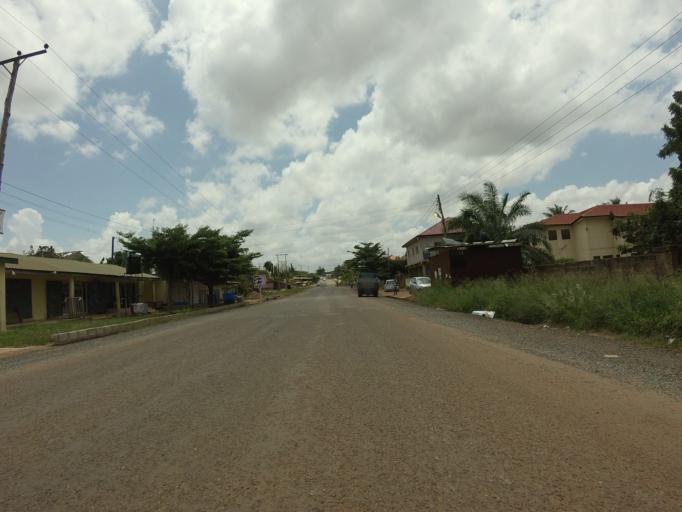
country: GH
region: Greater Accra
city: Medina Estates
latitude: 5.6811
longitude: -0.1978
